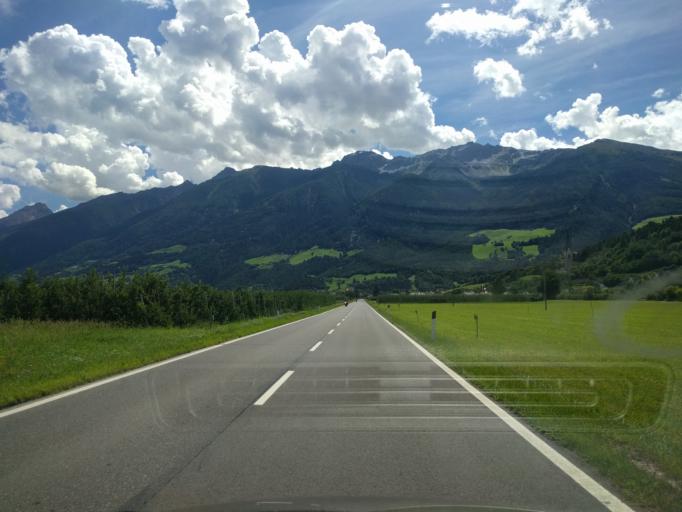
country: IT
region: Trentino-Alto Adige
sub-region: Bolzano
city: Prato Allo Stelvio
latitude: 46.6291
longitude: 10.5788
